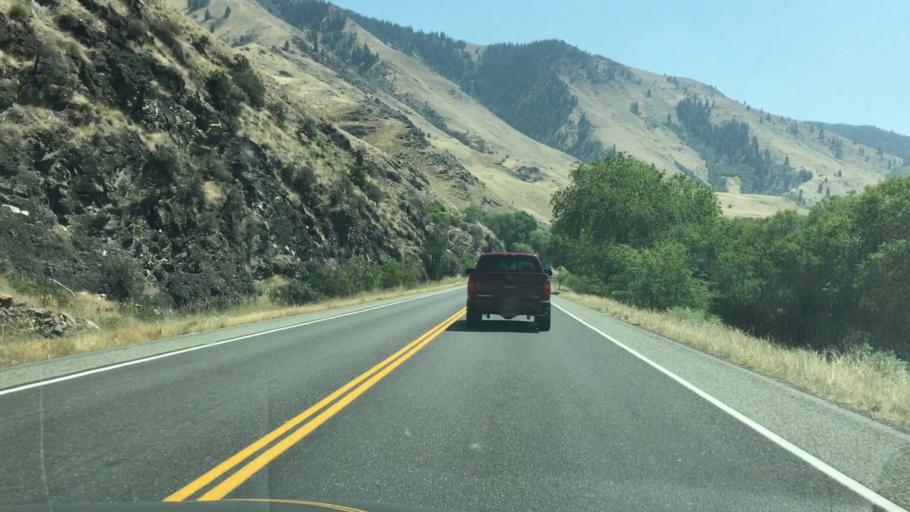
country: US
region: Idaho
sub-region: Valley County
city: McCall
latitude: 45.3457
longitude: -116.3531
